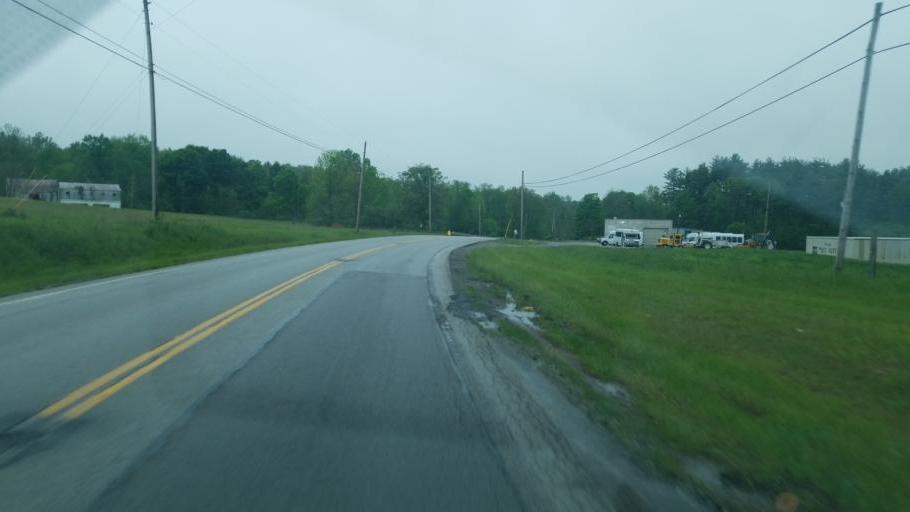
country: US
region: Ohio
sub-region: Highland County
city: Hillsboro
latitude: 39.2480
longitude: -83.6058
